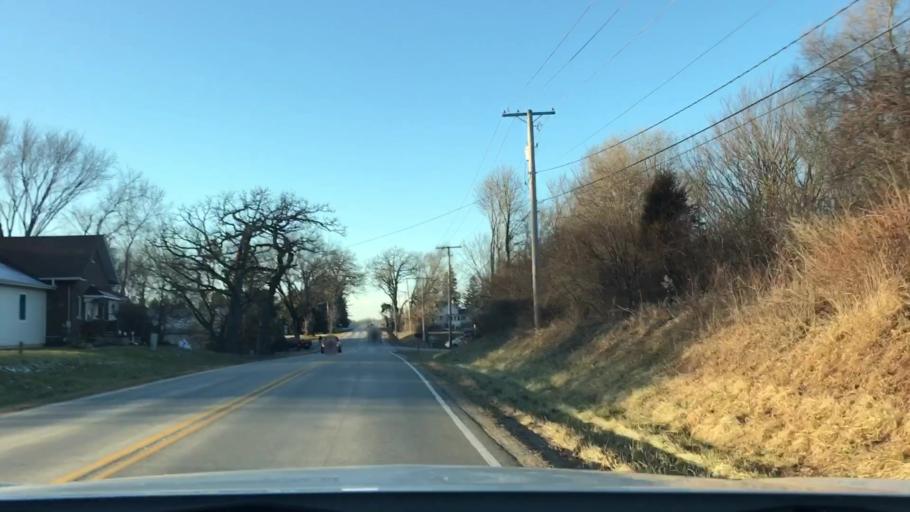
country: US
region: Illinois
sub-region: Kane County
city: Gilberts
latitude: 42.0815
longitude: -88.3833
